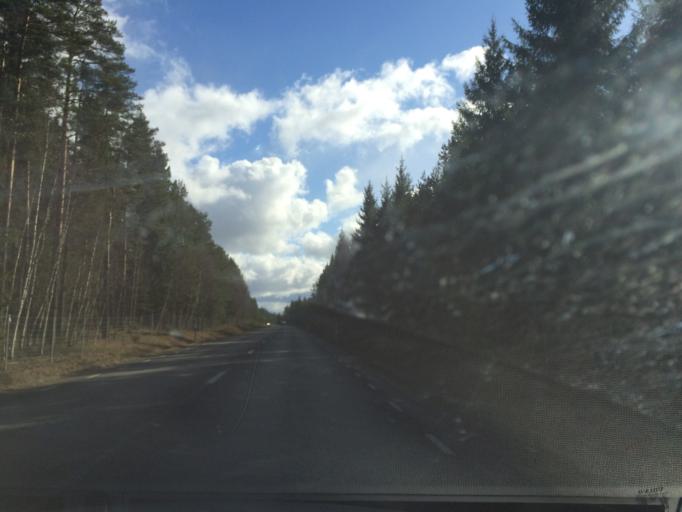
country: SE
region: Vaestra Goetaland
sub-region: Skara Kommun
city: Skara
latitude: 58.3631
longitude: 13.4215
